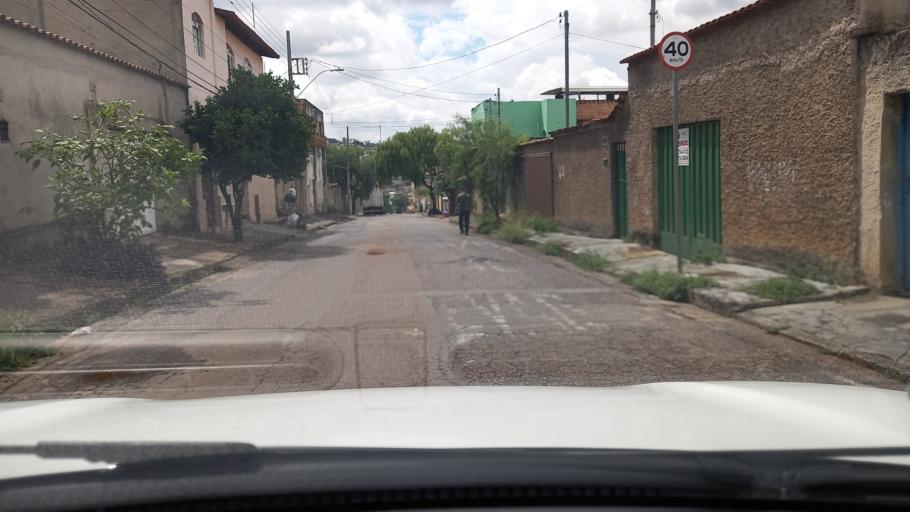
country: BR
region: Minas Gerais
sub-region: Contagem
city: Contagem
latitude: -19.8993
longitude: -44.0225
